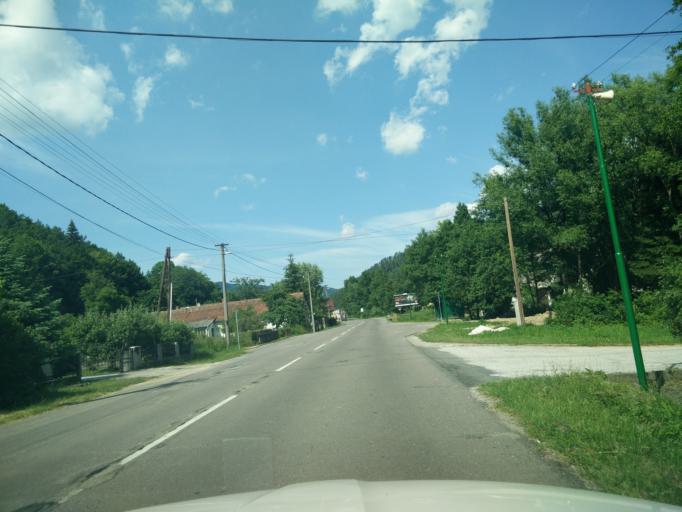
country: SK
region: Nitriansky
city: Prievidza
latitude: 48.9057
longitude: 18.6527
